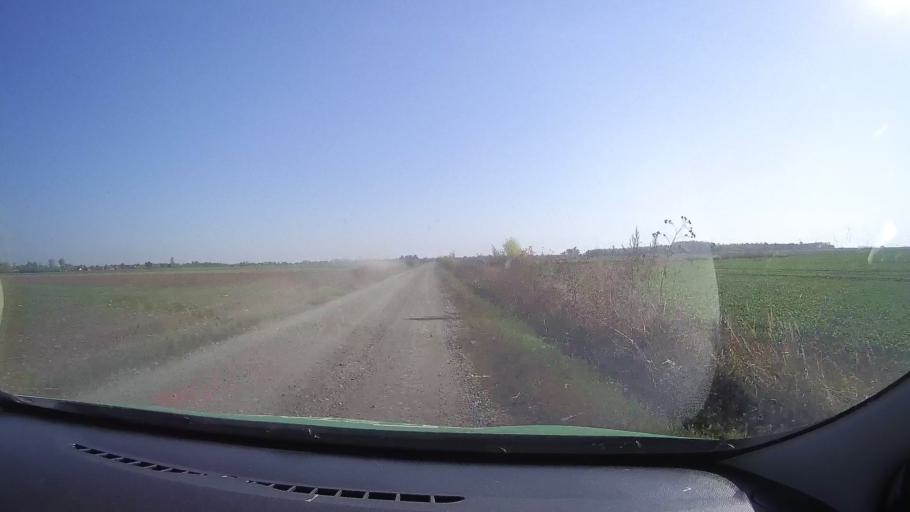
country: RO
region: Satu Mare
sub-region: Comuna Berveni
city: Berveni
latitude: 47.7349
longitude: 22.4556
